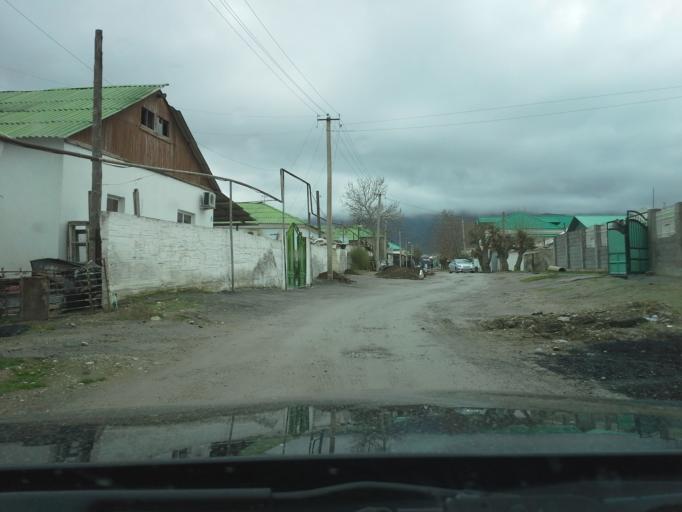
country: TM
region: Ahal
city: Abadan
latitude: 37.9615
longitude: 58.2211
